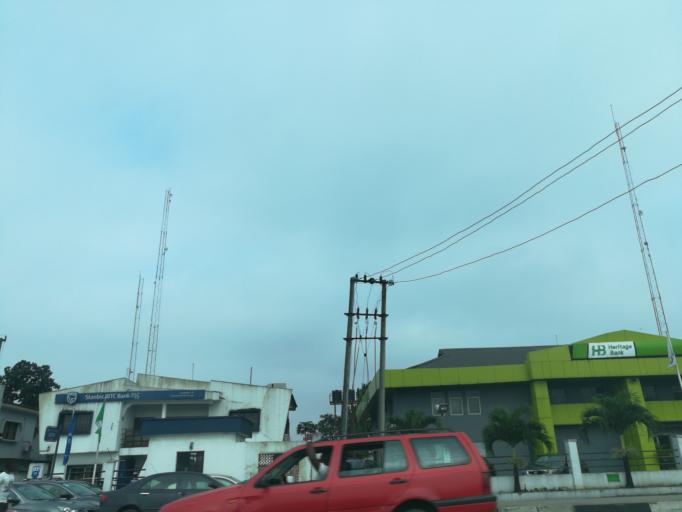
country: NG
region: Rivers
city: Port Harcourt
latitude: 4.8150
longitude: 7.0048
